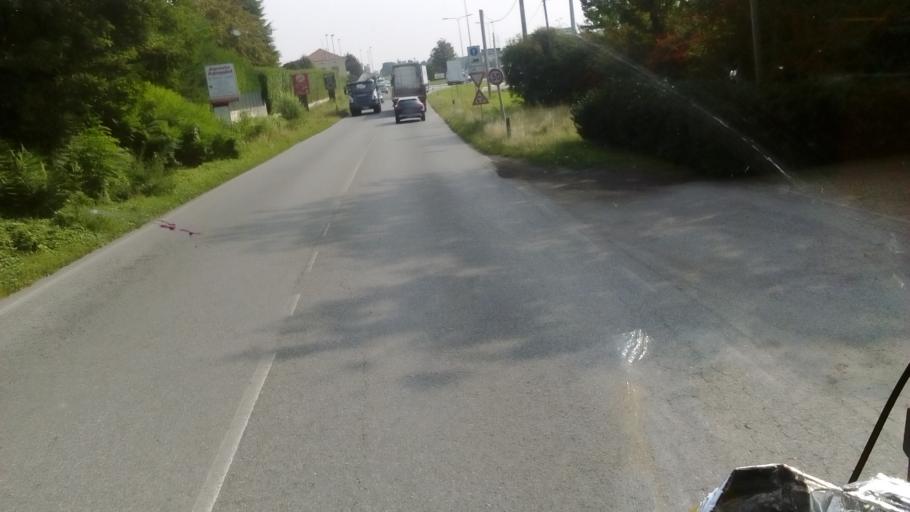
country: IT
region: Lombardy
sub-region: Provincia di Como
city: Cermenate
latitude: 45.6948
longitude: 9.0770
